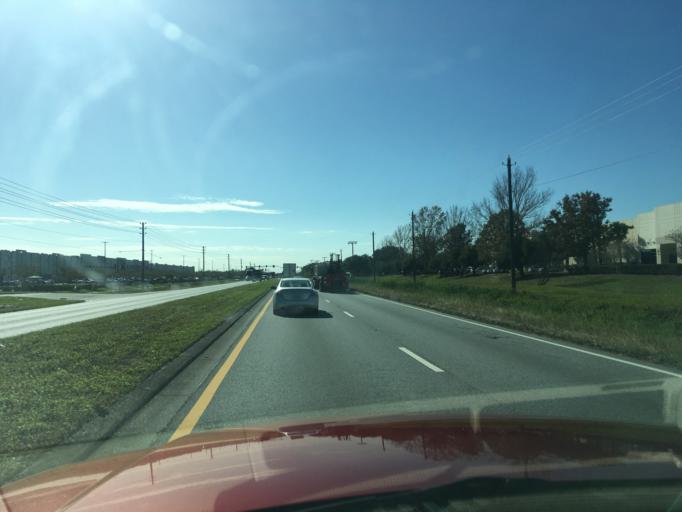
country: US
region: Florida
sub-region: Polk County
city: Winston
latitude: 28.0233
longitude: -82.0557
